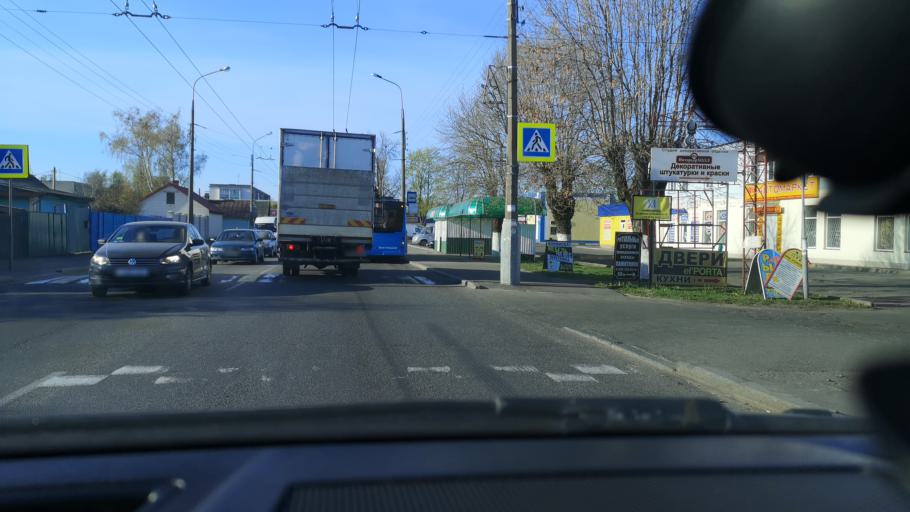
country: BY
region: Gomel
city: Gomel
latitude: 52.4242
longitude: 30.9737
